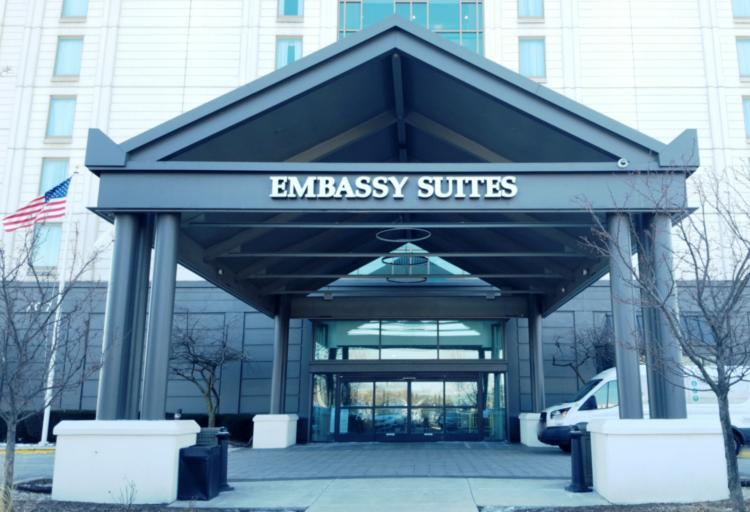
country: US
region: Illinois
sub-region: DuPage County
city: Downers Grove
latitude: 41.8386
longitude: -87.9995
